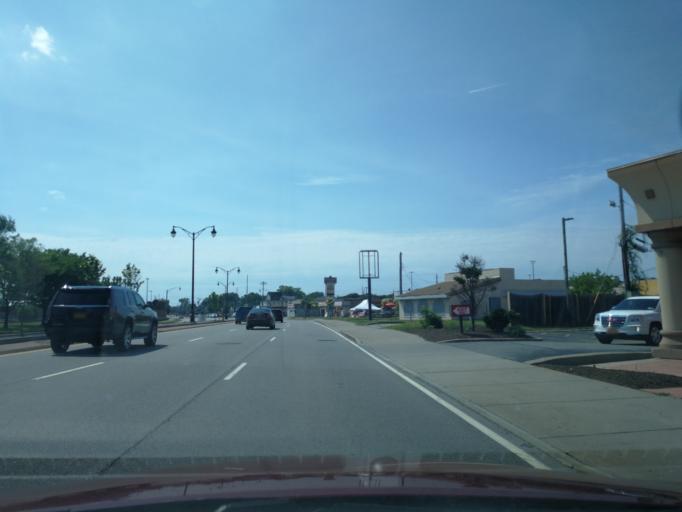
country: US
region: New York
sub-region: Monroe County
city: Greece
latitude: 43.2020
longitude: -77.6424
